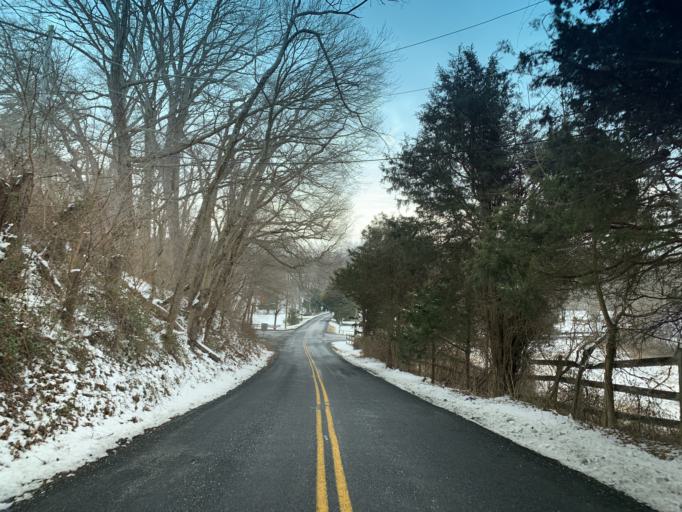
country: US
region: Pennsylvania
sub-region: York County
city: Susquehanna Trails
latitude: 39.7079
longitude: -76.2996
